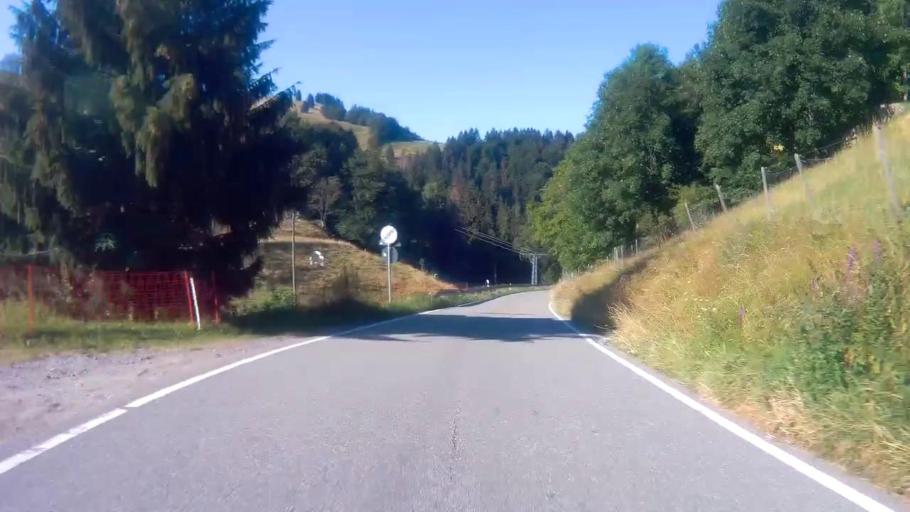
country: DE
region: Baden-Wuerttemberg
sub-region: Freiburg Region
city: Horben
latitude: 47.8920
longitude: 7.8747
